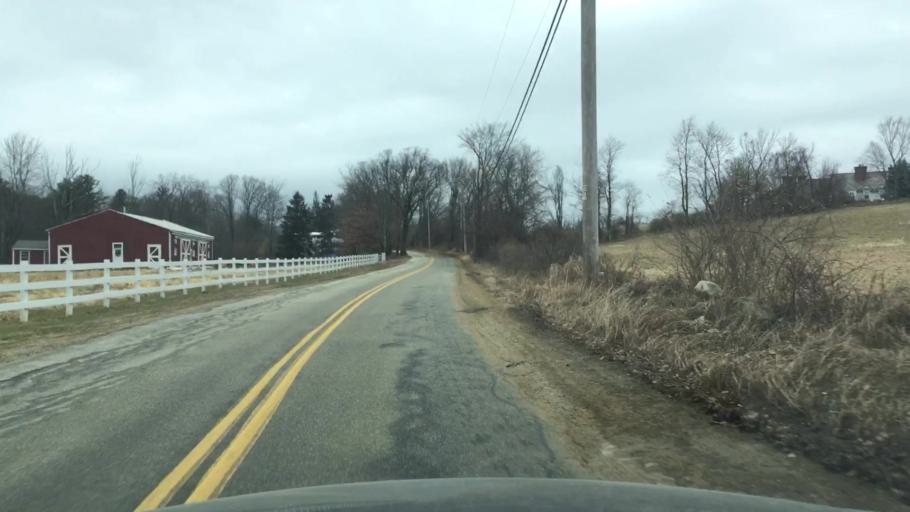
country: US
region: New Hampshire
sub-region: Hillsborough County
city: Mont Vernon
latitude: 42.9316
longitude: -71.6081
